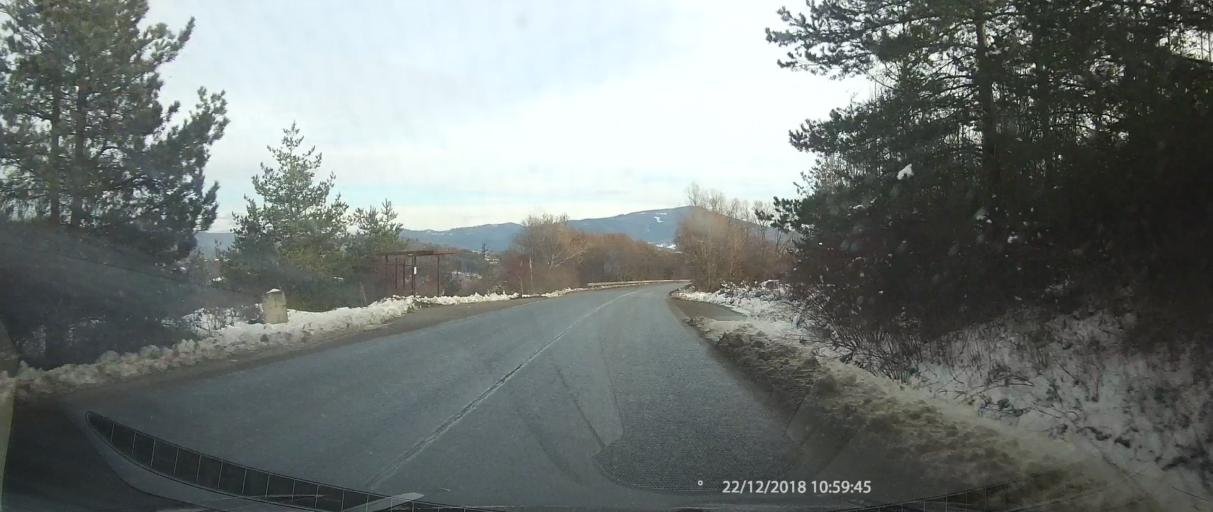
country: MK
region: Kriva Palanka
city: Kriva Palanka
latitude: 42.2290
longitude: 22.4848
